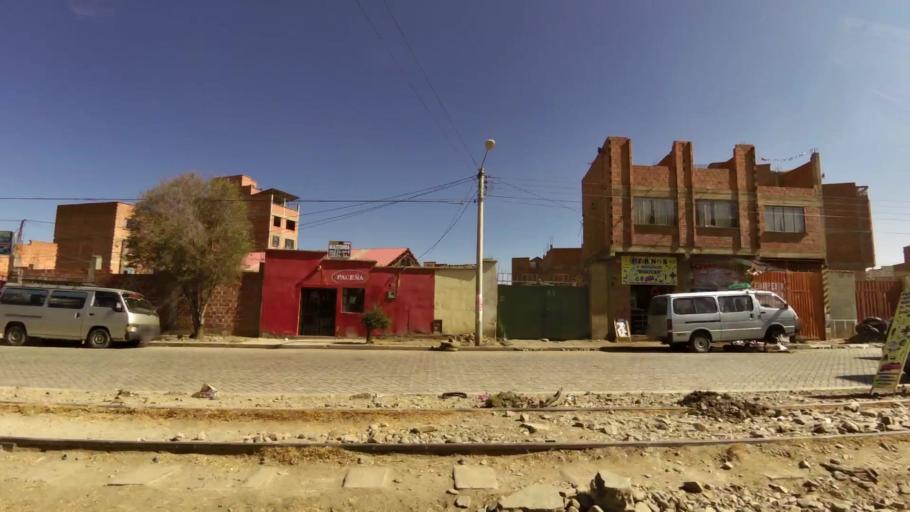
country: BO
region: La Paz
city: La Paz
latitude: -16.5189
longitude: -68.1580
